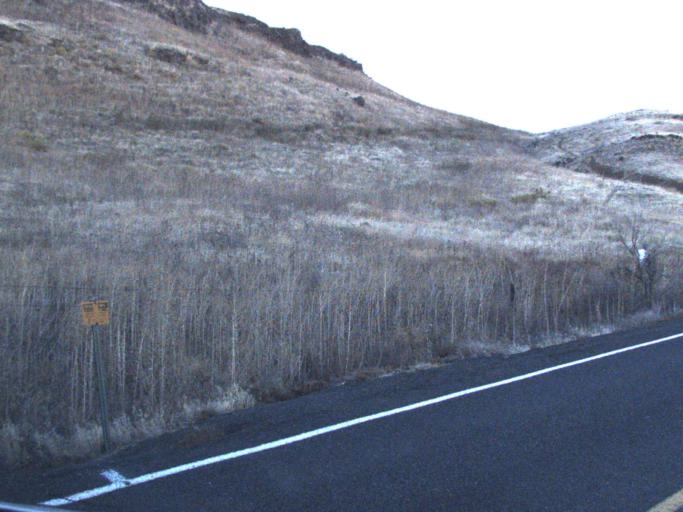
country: US
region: Washington
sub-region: Walla Walla County
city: Waitsburg
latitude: 46.6153
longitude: -118.2302
